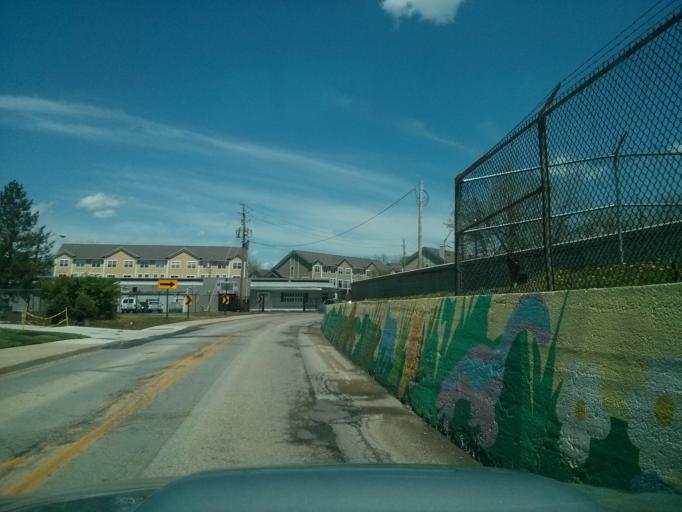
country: US
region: Indiana
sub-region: Marion County
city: Broad Ripple
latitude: 39.8741
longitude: -86.1414
